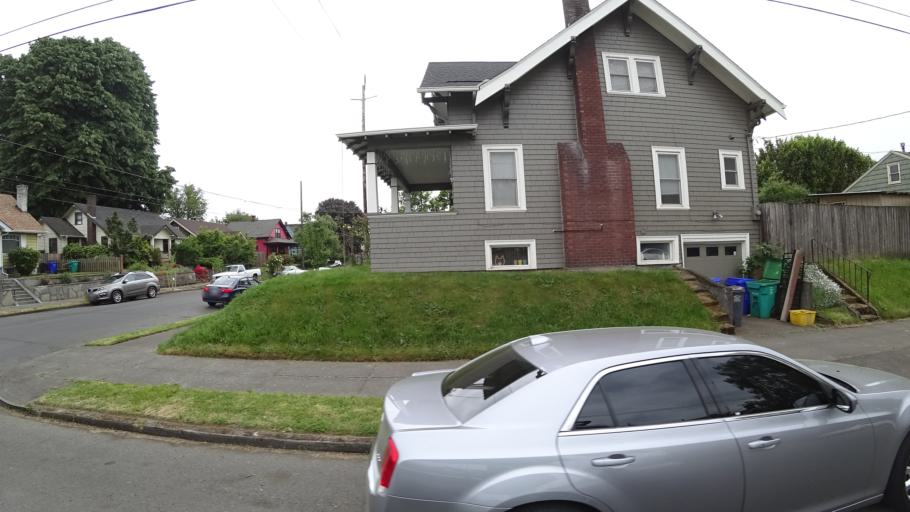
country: US
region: Oregon
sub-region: Multnomah County
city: Portland
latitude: 45.5520
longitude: -122.6639
